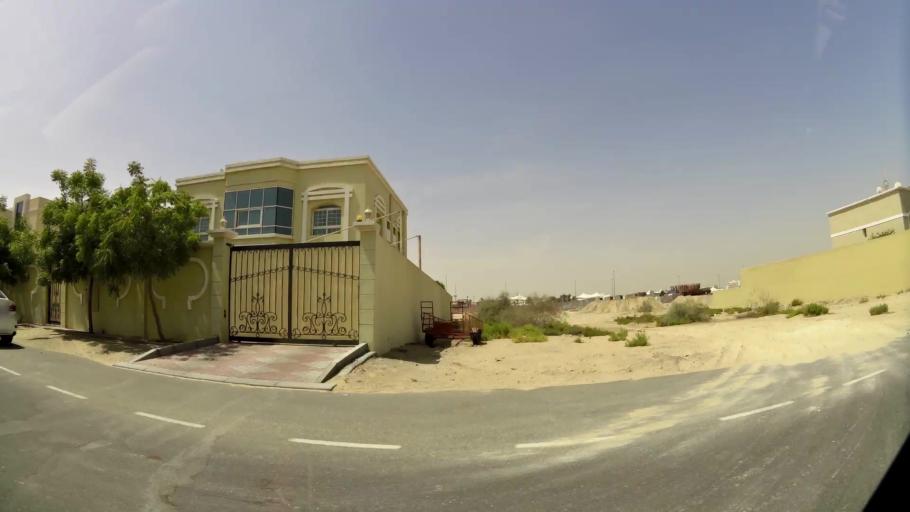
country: AE
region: Ash Shariqah
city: Sharjah
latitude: 25.1778
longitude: 55.4192
